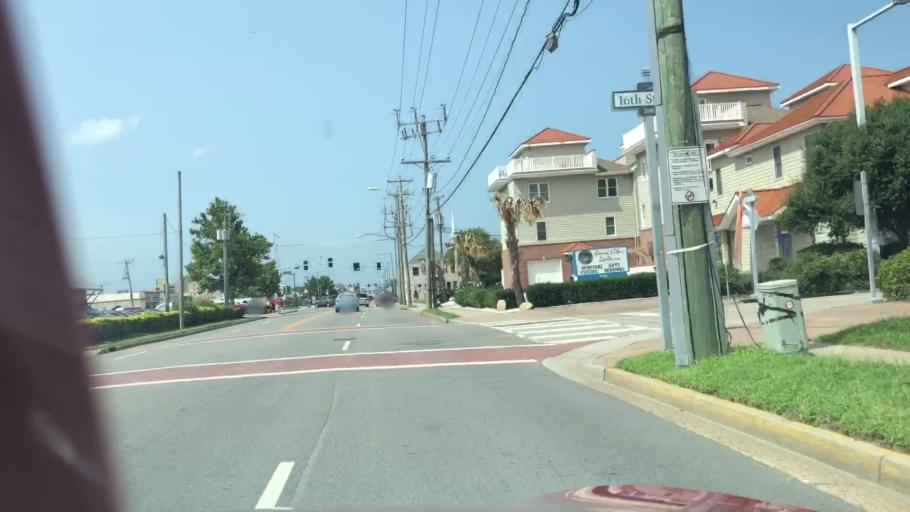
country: US
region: Virginia
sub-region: City of Virginia Beach
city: Virginia Beach
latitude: 36.8440
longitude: -75.9752
